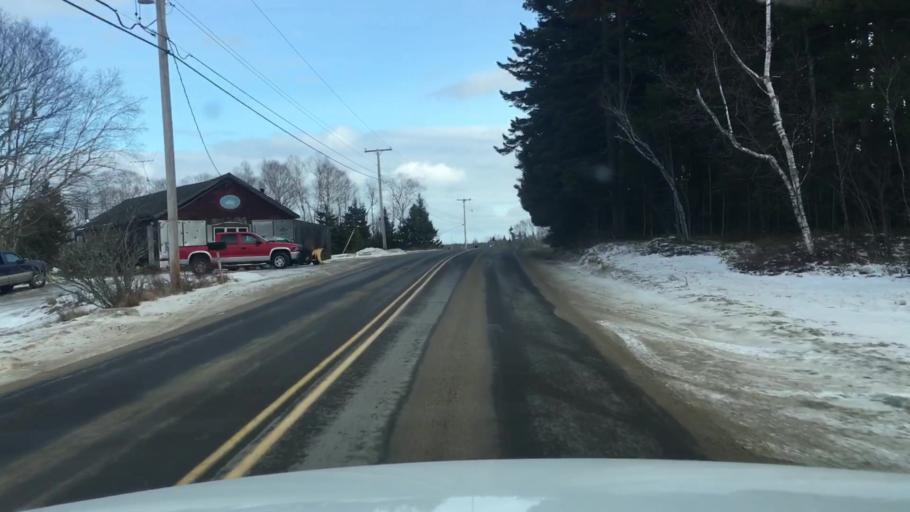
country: US
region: Maine
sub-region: Washington County
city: Jonesport
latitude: 44.6086
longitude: -67.5991
